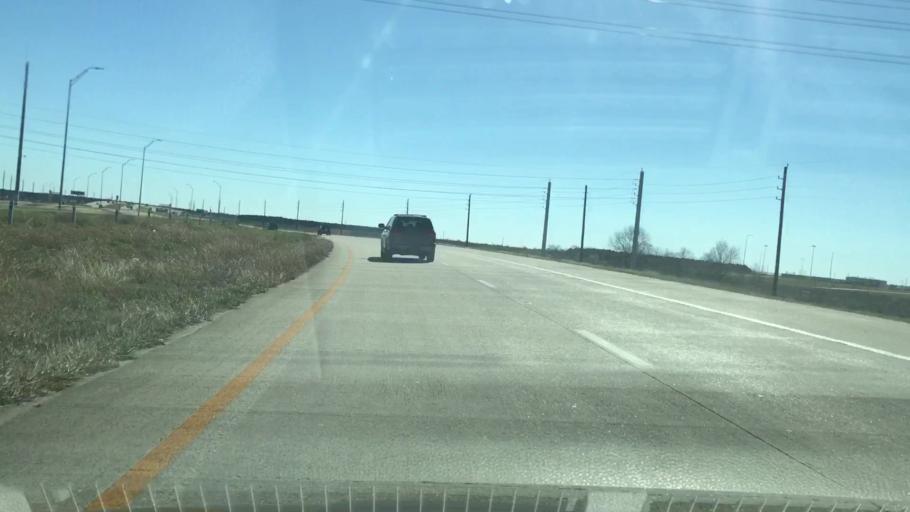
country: US
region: Texas
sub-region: Harris County
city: Cypress
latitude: 29.9132
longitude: -95.7621
